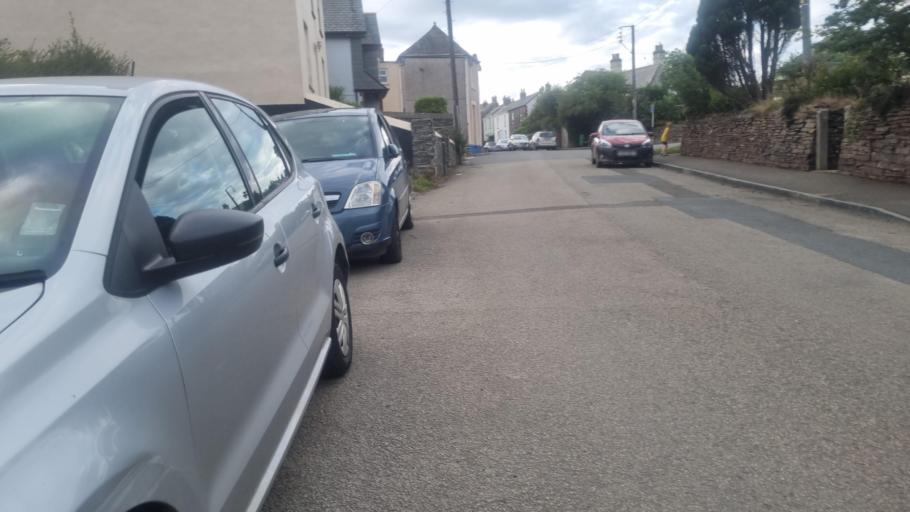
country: GB
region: England
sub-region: Cornwall
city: Tintagel
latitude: 50.6218
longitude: -4.7296
